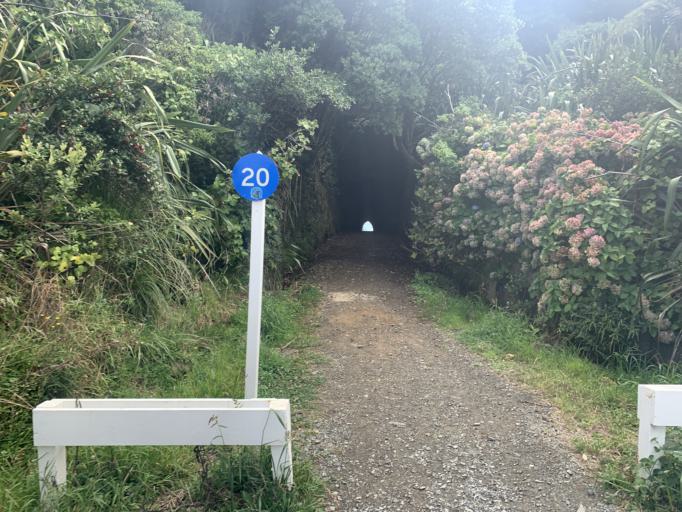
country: NZ
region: Waikato
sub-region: Otorohanga District
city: Otorohanga
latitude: -38.4766
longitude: 174.6400
